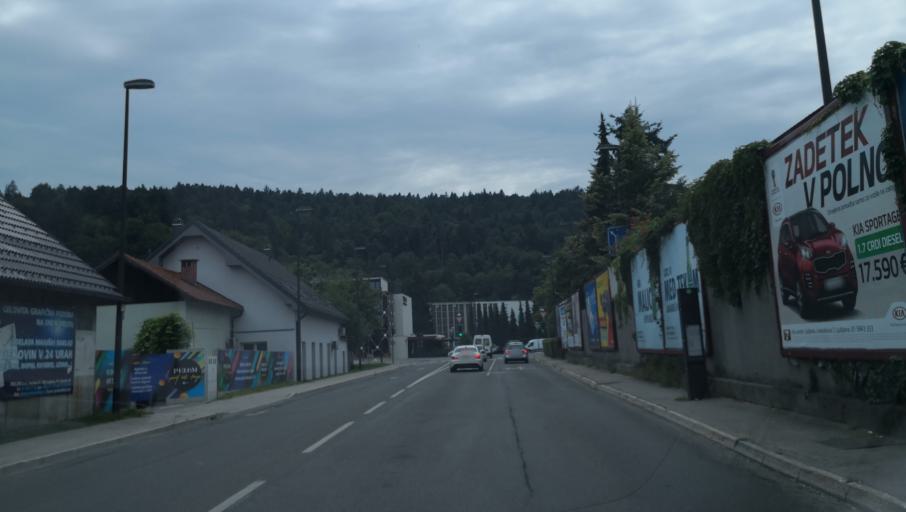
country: SI
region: Medvode
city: Zgornje Pirnice
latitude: 46.1008
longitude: 14.4607
